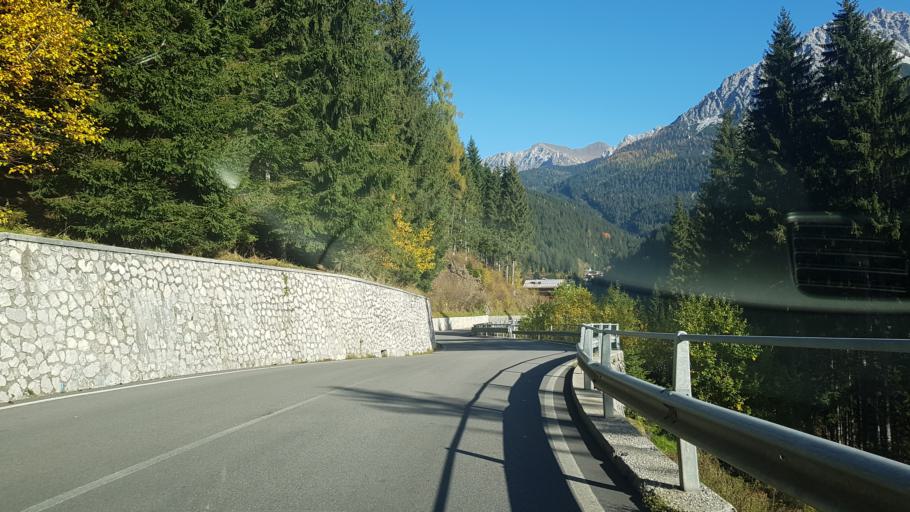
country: IT
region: Veneto
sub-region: Provincia di Belluno
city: Candide
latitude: 46.5970
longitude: 12.5216
